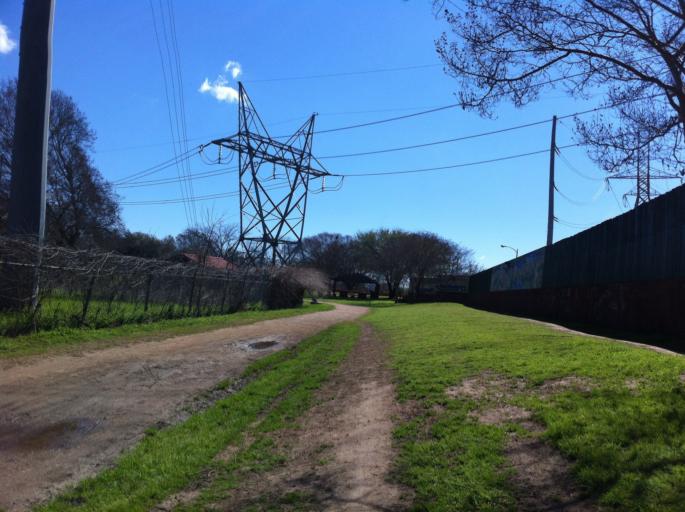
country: US
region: Texas
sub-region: Travis County
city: Austin
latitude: 30.2513
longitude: -97.7197
